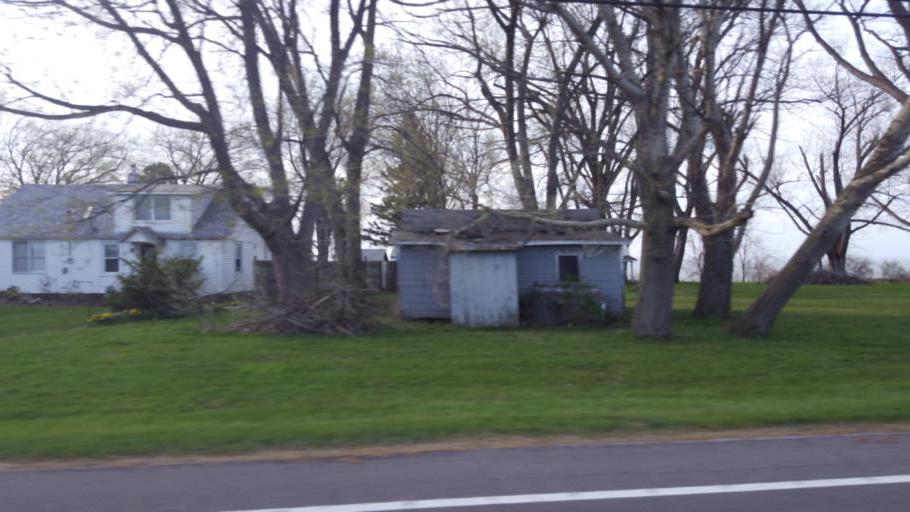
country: US
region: Ohio
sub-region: Lorain County
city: Vermilion
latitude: 41.3955
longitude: -82.4330
